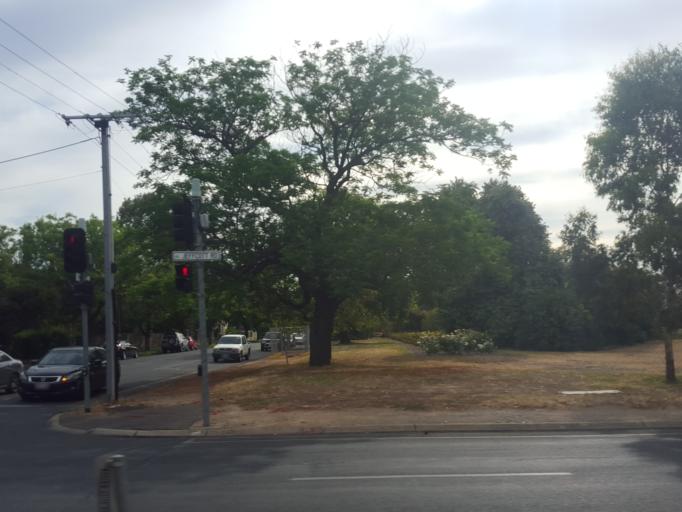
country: AU
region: South Australia
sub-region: Adelaide
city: North Adelaide
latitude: -34.9028
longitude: 138.5900
